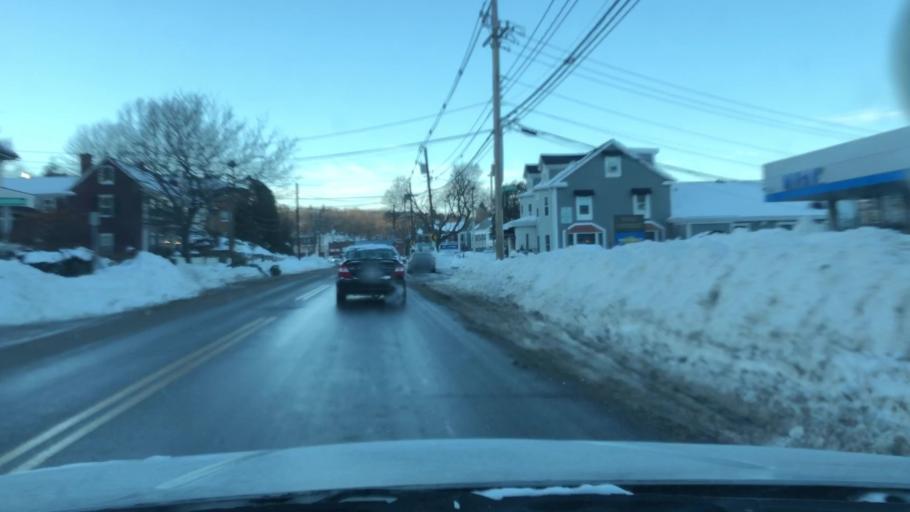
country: US
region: Massachusetts
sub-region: Middlesex County
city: Arlington
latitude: 42.4223
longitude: -71.1732
